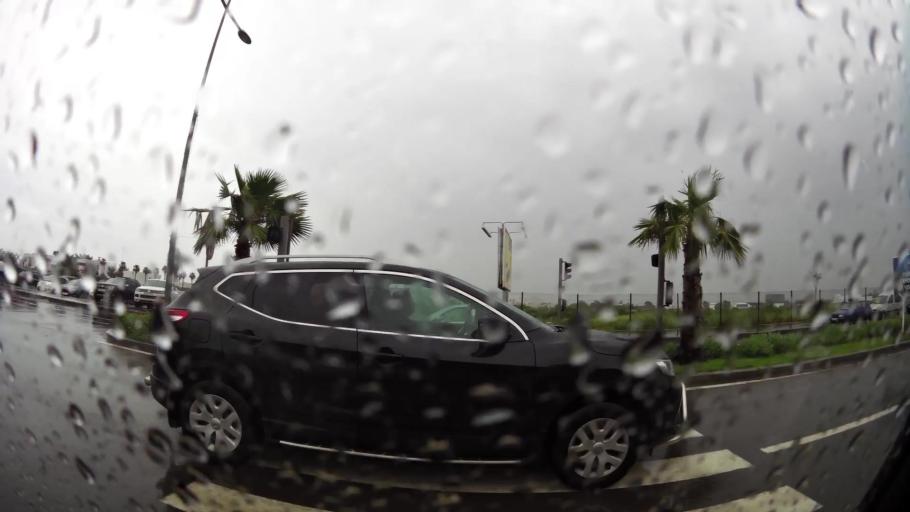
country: MA
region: Grand Casablanca
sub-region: Casablanca
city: Casablanca
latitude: 33.5540
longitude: -7.6661
